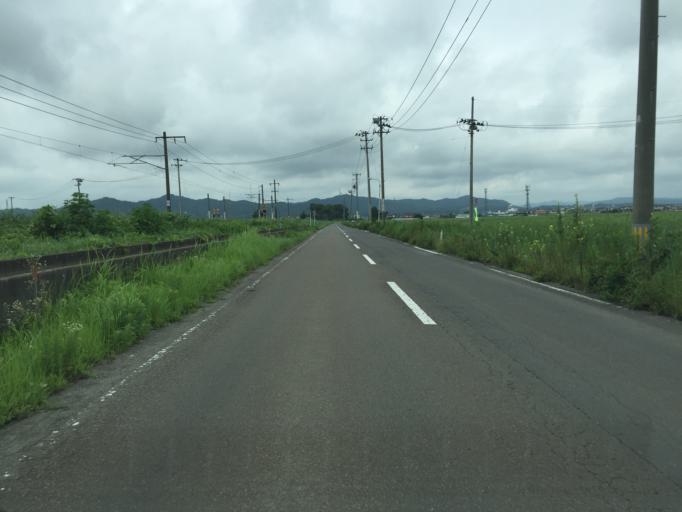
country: JP
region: Miyagi
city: Watari
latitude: 38.0272
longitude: 140.8735
